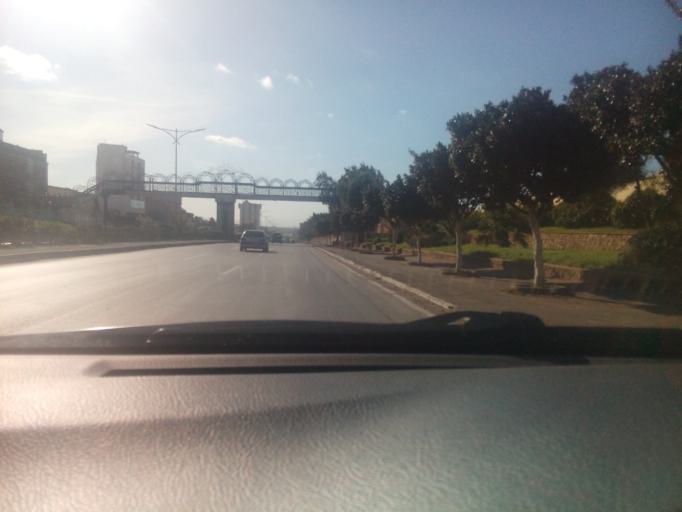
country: DZ
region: Oran
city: Oran
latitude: 35.6946
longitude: -0.6053
